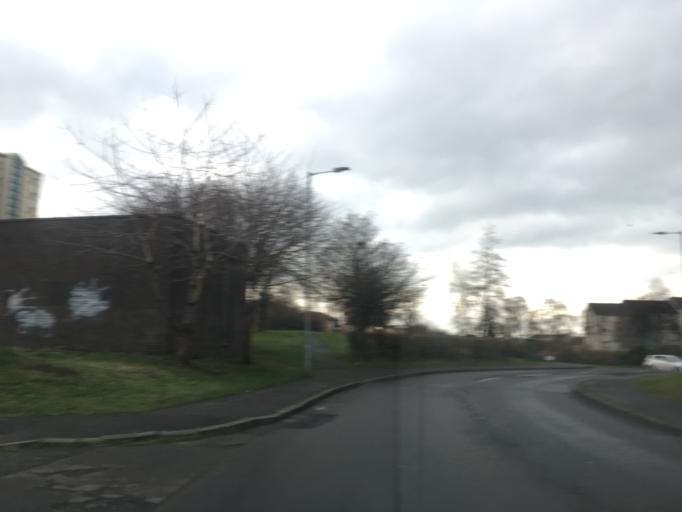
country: GB
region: Scotland
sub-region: Edinburgh
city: Colinton
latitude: 55.9179
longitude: -3.2744
